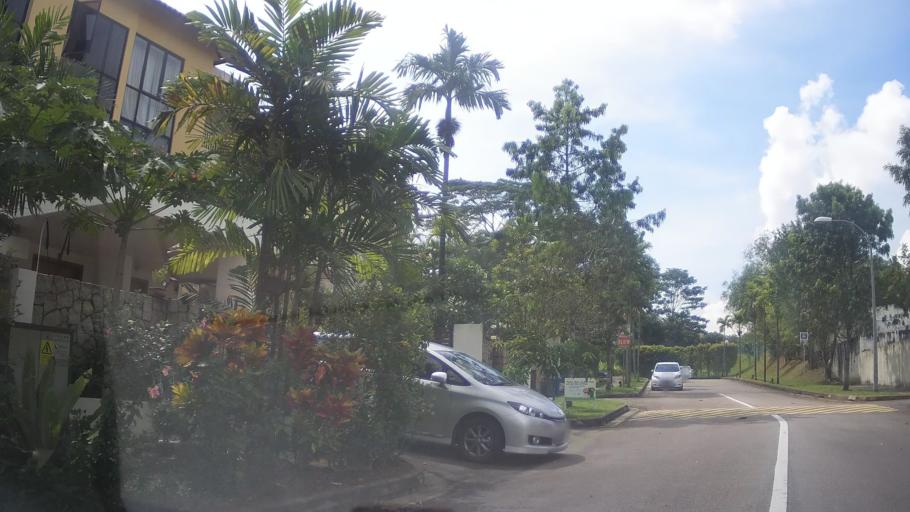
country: MY
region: Johor
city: Johor Bahru
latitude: 1.4163
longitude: 103.7555
